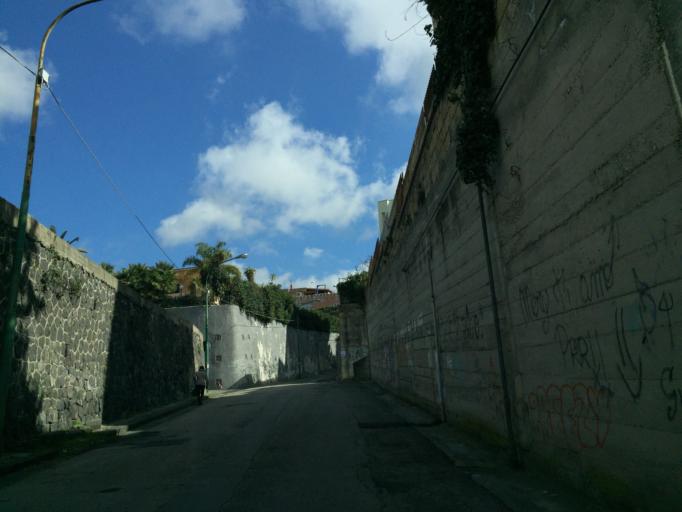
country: IT
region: Campania
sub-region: Provincia di Napoli
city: Massa di Somma
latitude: 40.8426
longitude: 14.3710
